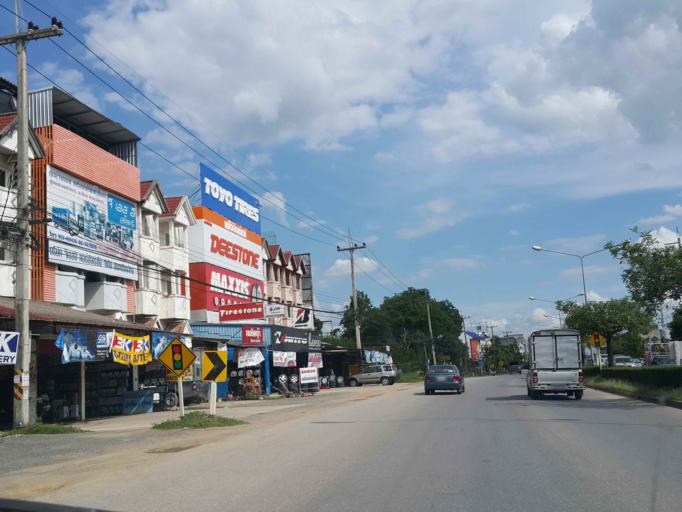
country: TH
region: Chiang Mai
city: San Sai
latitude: 18.8885
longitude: 99.0129
